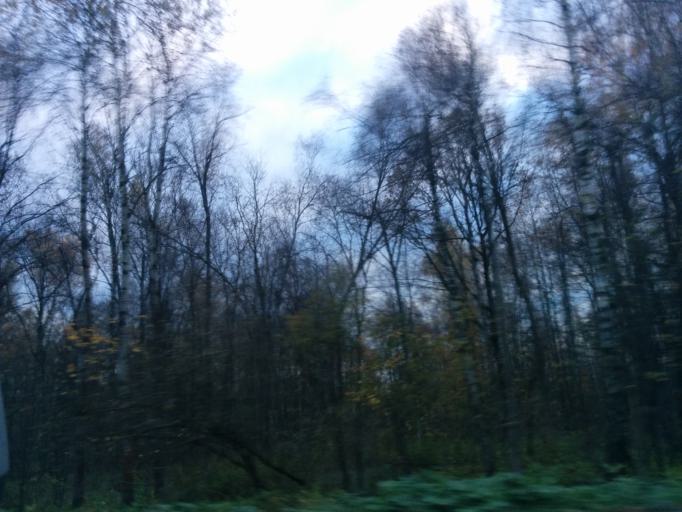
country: RU
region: Moskovskaya
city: Biryulevo Zapadnoye
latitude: 55.5419
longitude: 37.6264
